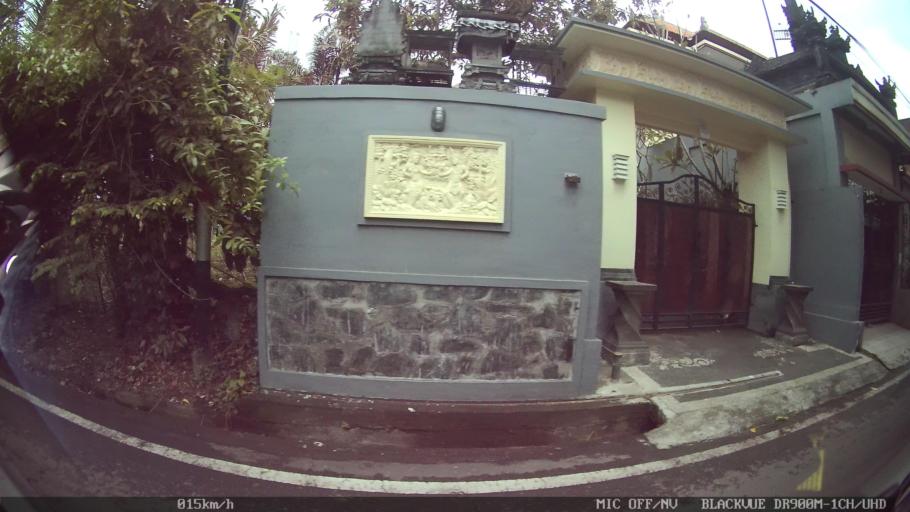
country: ID
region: Bali
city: Banjar Parekan
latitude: -8.5643
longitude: 115.2126
